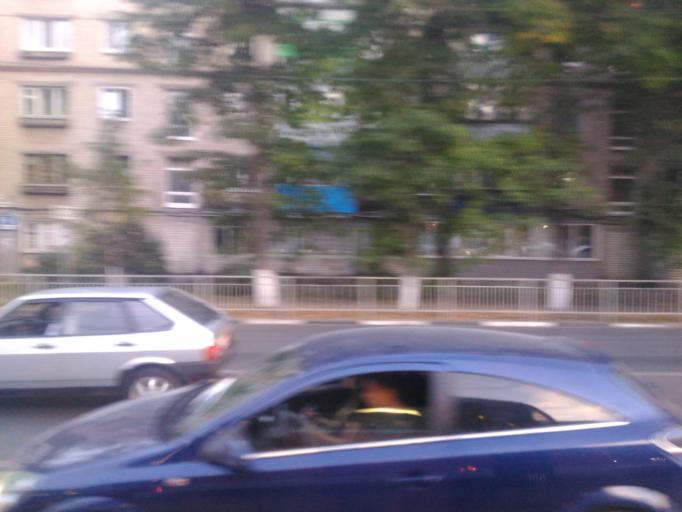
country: RU
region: Ulyanovsk
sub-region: Ulyanovskiy Rayon
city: Ulyanovsk
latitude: 54.2902
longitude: 48.3084
